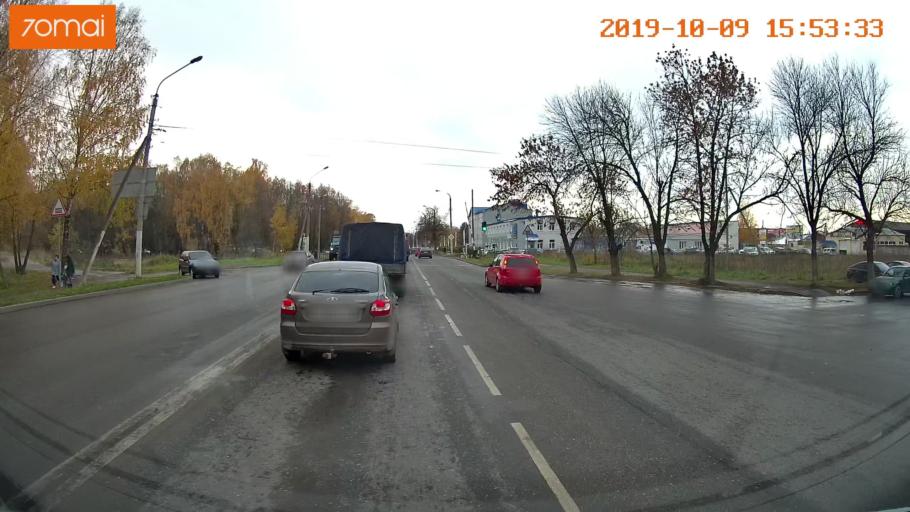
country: RU
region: Kostroma
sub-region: Kostromskoy Rayon
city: Kostroma
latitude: 57.7850
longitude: 40.9613
